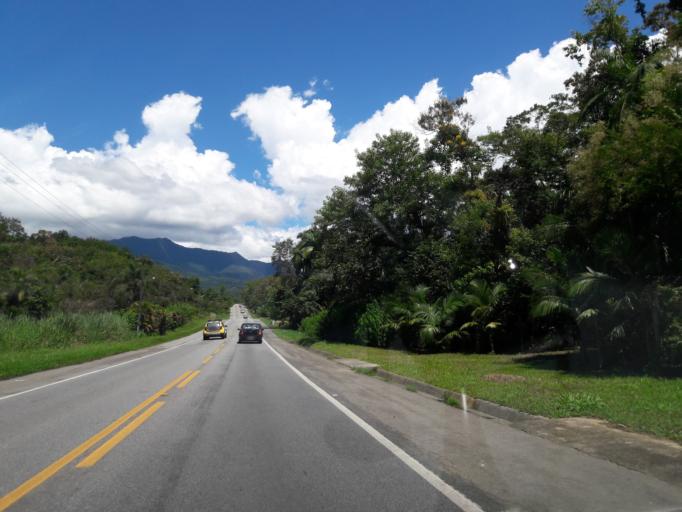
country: BR
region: Parana
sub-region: Antonina
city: Antonina
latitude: -25.5304
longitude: -48.7945
